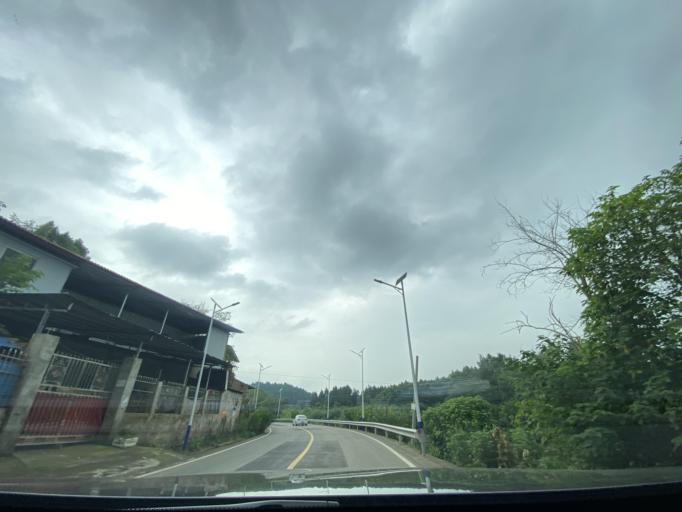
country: CN
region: Sichuan
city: Jiancheng
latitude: 30.5529
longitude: 104.5228
